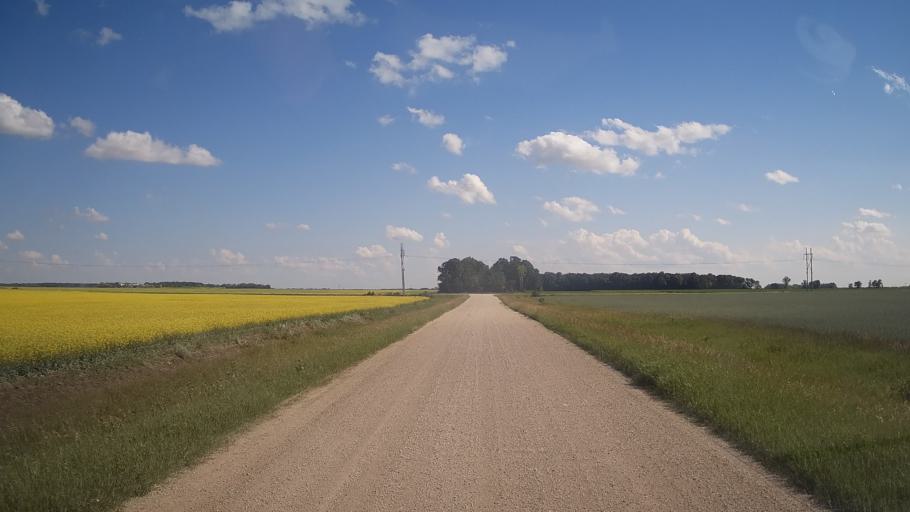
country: CA
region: Manitoba
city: Stonewall
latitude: 50.1251
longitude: -97.5054
